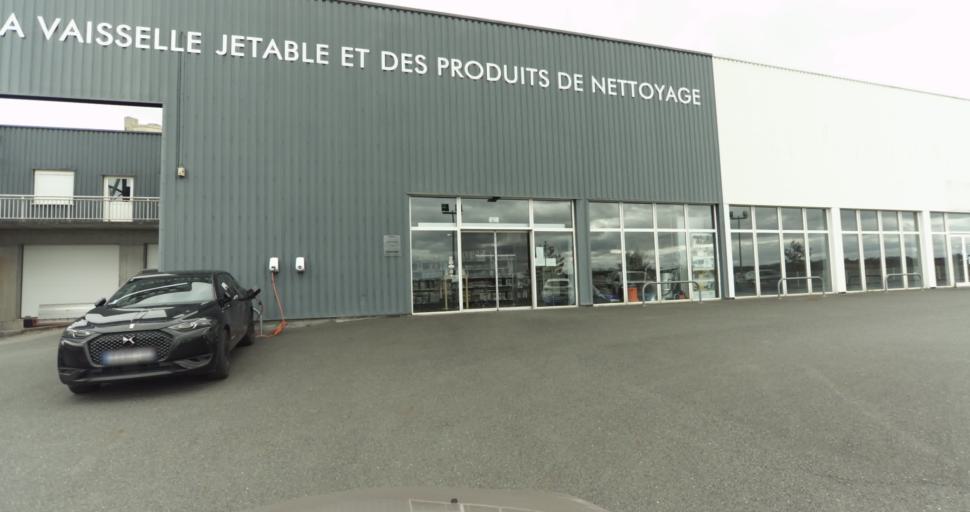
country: FR
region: Midi-Pyrenees
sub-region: Departement du Tarn
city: Puygouzon
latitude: 43.8941
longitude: 2.1657
